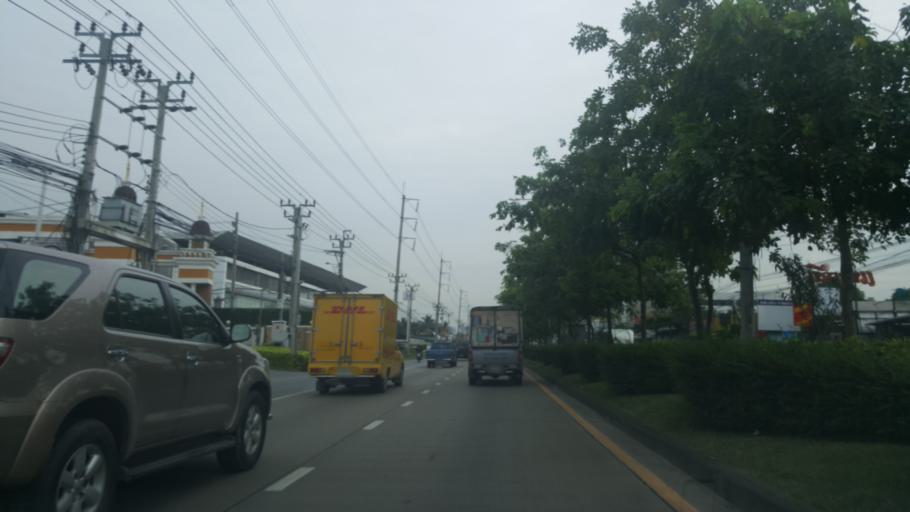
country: TH
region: Bangkok
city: Phasi Charoen
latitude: 13.6983
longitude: 100.4410
